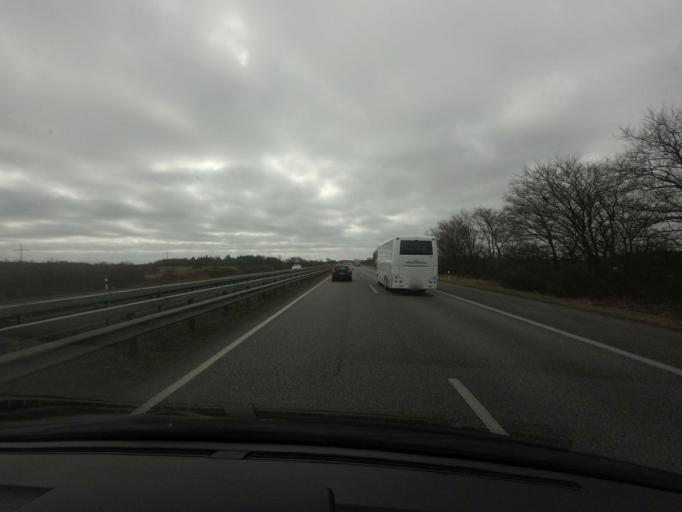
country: DE
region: Schleswig-Holstein
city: Bollingstedt
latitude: 54.6300
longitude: 9.4402
